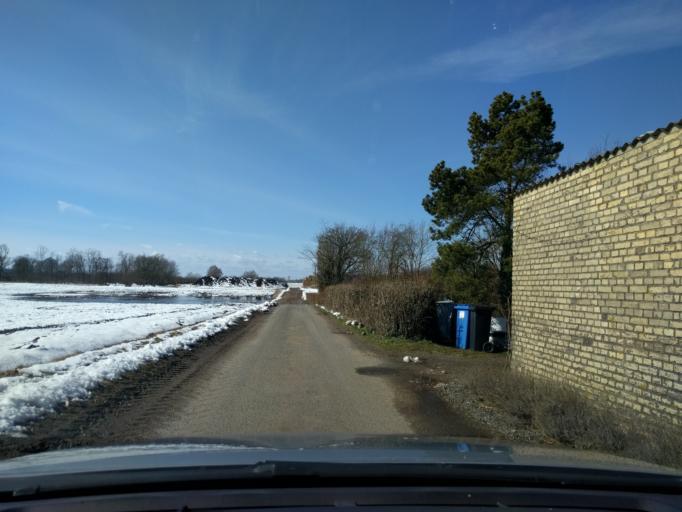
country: DK
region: South Denmark
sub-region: Nyborg Kommune
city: Ullerslev
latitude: 55.3707
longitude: 10.7226
